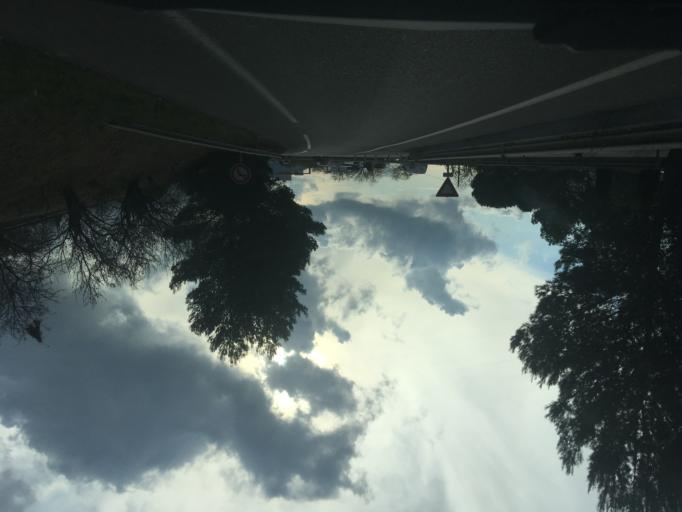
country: FR
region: Provence-Alpes-Cote d'Azur
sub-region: Departement du Var
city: Cuers
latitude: 43.2231
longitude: 6.0700
